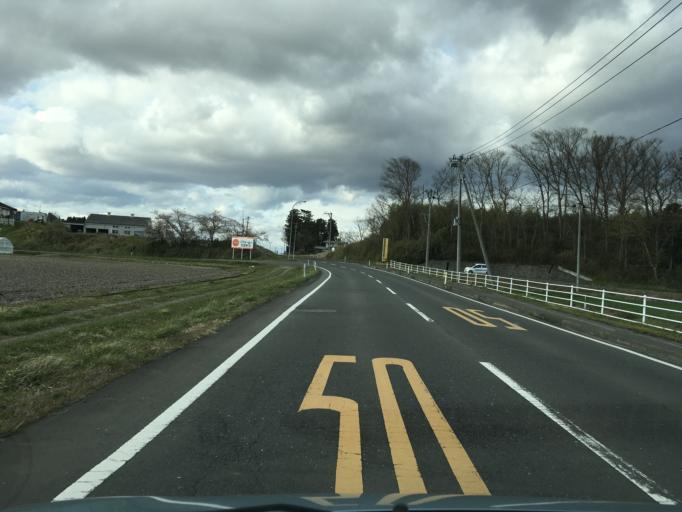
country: JP
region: Miyagi
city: Wakuya
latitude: 38.6513
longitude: 141.1915
